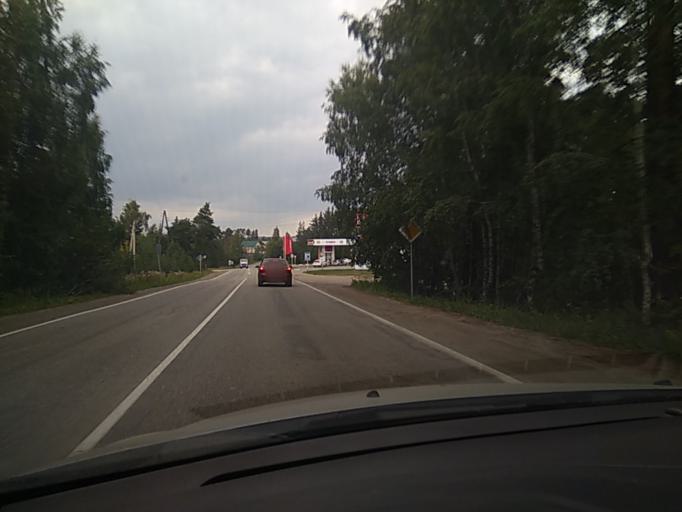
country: RU
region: Chelyabinsk
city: Kyshtym
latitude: 55.7178
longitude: 60.5107
